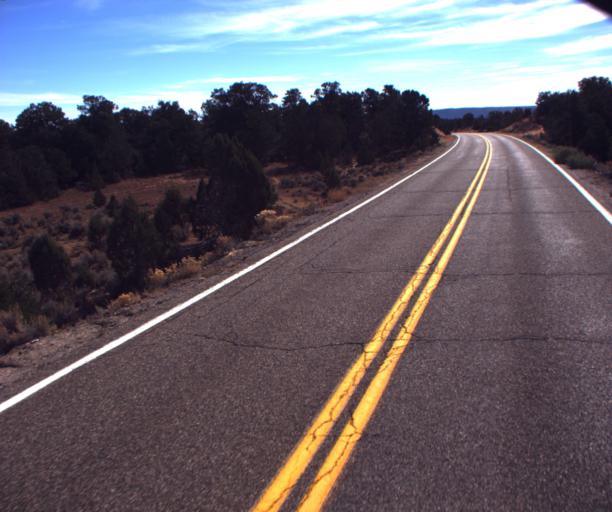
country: US
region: Arizona
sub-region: Navajo County
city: Kayenta
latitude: 36.6466
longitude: -110.5176
